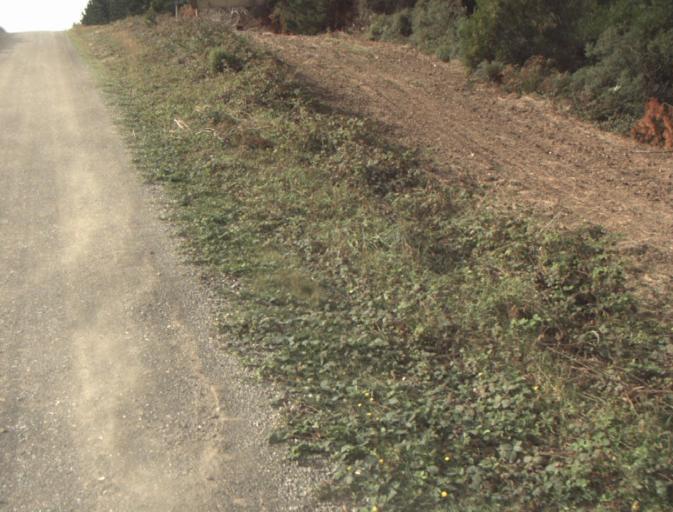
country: AU
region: Tasmania
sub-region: Launceston
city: Mayfield
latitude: -41.1862
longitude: 147.1784
